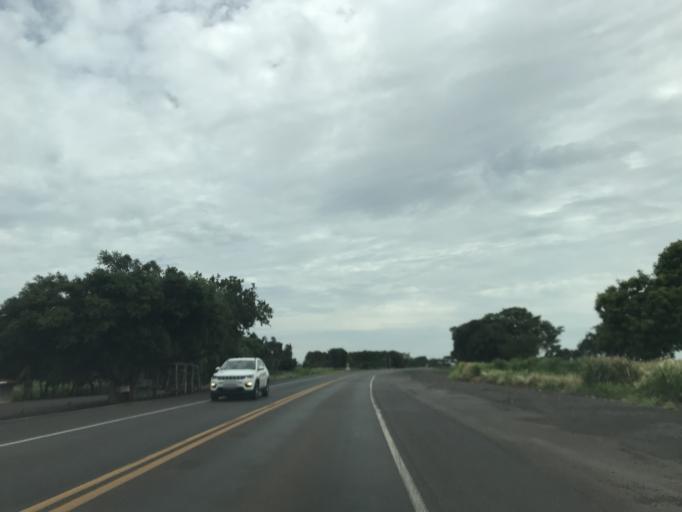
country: BR
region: Minas Gerais
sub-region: Frutal
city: Frutal
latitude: -20.1335
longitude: -49.1097
